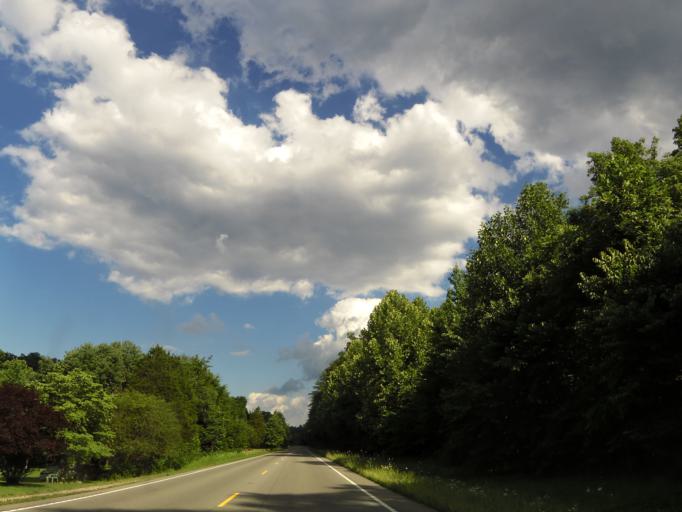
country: US
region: Tennessee
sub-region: Lewis County
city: Hohenwald
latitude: 35.5907
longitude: -87.6885
